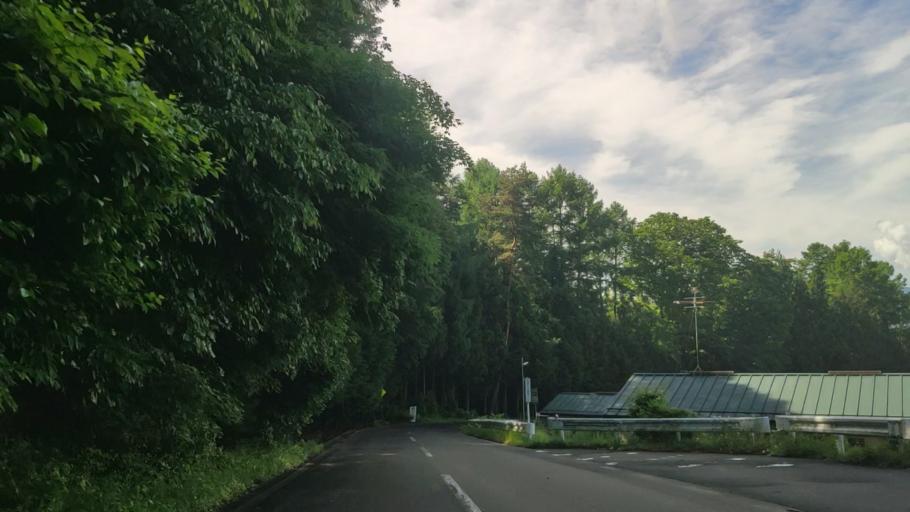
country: JP
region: Nagano
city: Suwa
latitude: 36.0713
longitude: 138.1357
